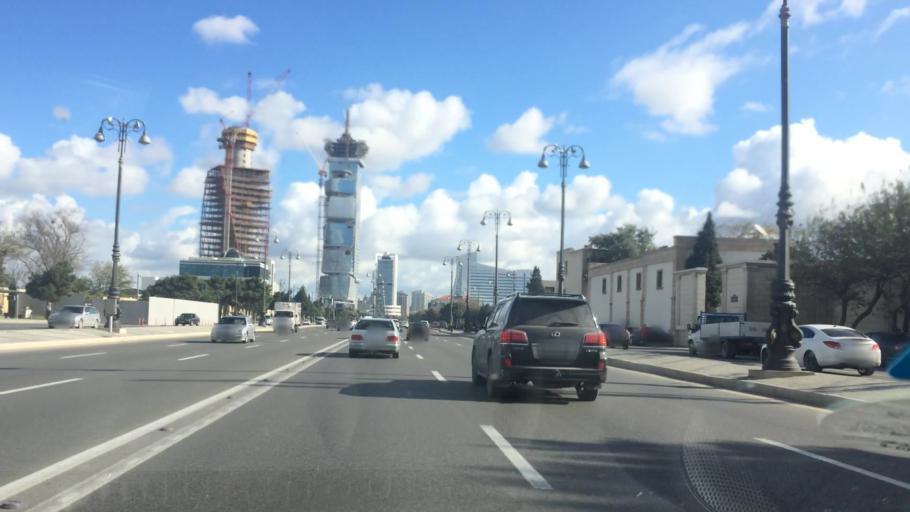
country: AZ
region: Baki
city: Baku
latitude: 40.4062
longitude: 49.8896
